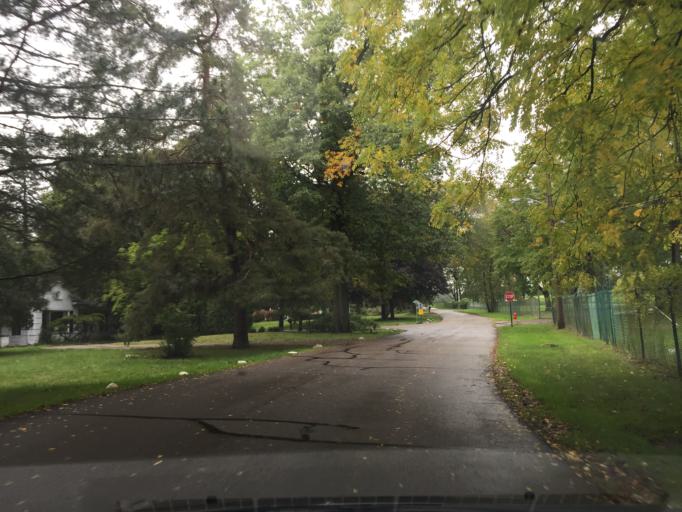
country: US
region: Michigan
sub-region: Oakland County
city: Bingham Farms
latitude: 42.5379
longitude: -83.2676
